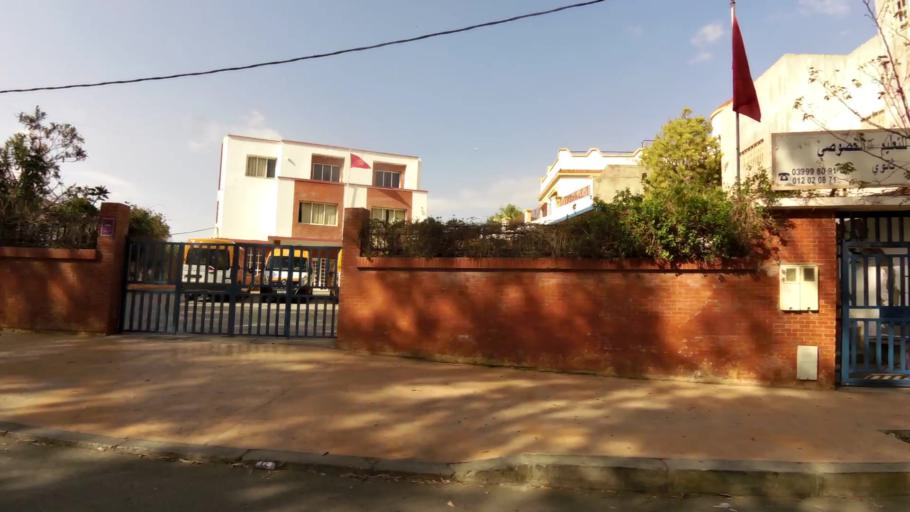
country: MA
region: Tanger-Tetouan
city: Tetouan
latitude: 35.5958
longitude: -5.3412
